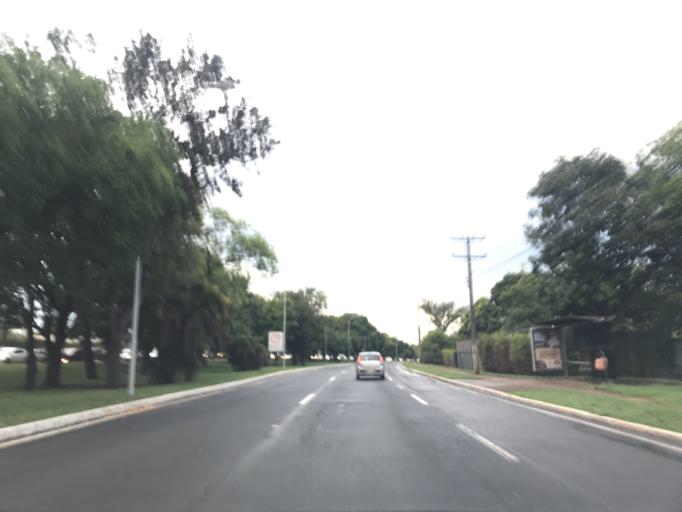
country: BR
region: Federal District
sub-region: Brasilia
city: Brasilia
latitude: -15.8495
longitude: -47.8753
